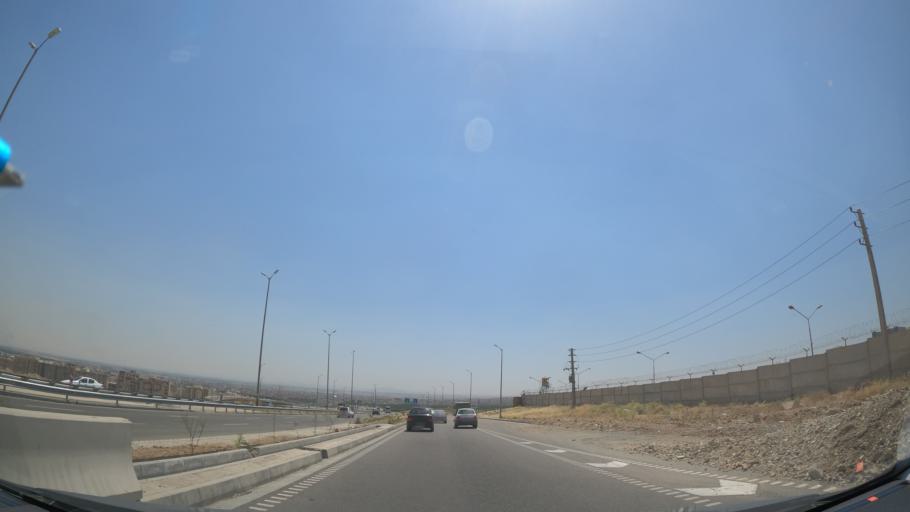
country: IR
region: Tehran
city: Shahr-e Qods
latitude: 35.7468
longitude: 51.1286
